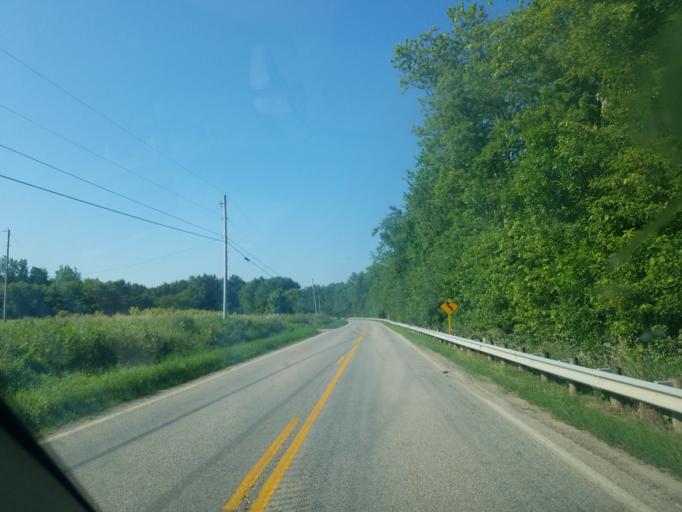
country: US
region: Ohio
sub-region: Marion County
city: Prospect
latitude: 40.4676
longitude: -83.1913
